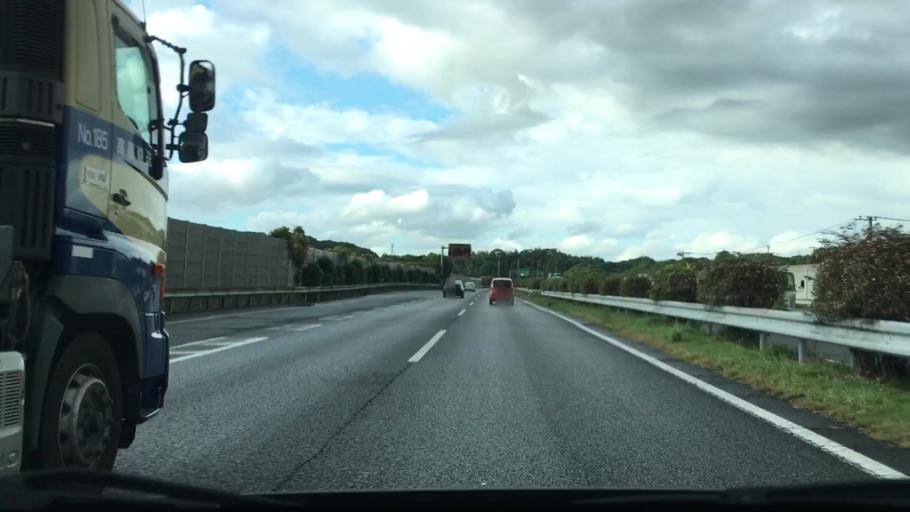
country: JP
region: Fukuoka
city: Koga
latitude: 33.7126
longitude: 130.4897
